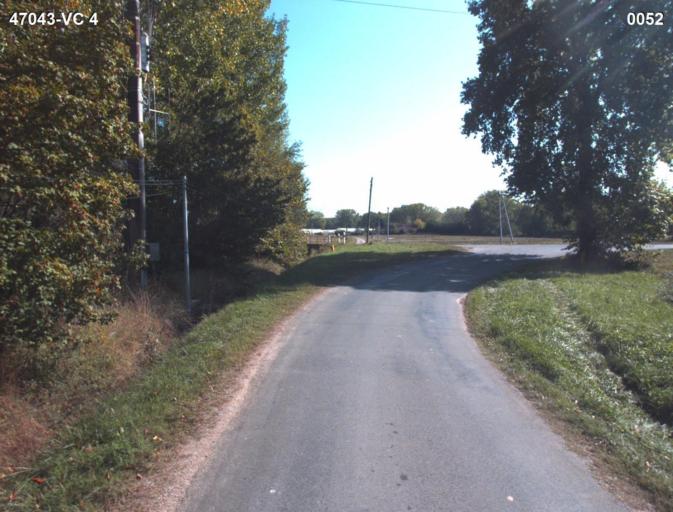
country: FR
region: Aquitaine
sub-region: Departement du Lot-et-Garonne
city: Buzet-sur-Baise
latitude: 44.2593
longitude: 0.3073
